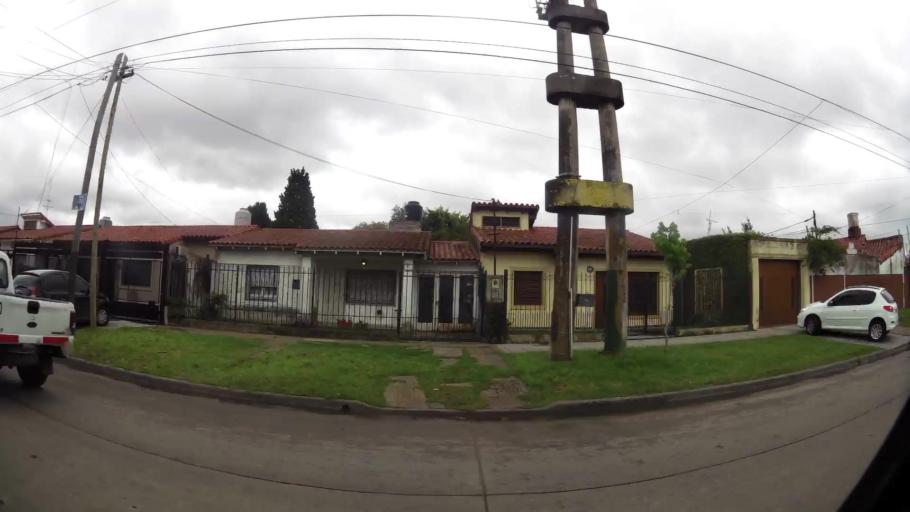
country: AR
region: Buenos Aires
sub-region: Partido de Lomas de Zamora
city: Lomas de Zamora
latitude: -34.7478
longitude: -58.3710
